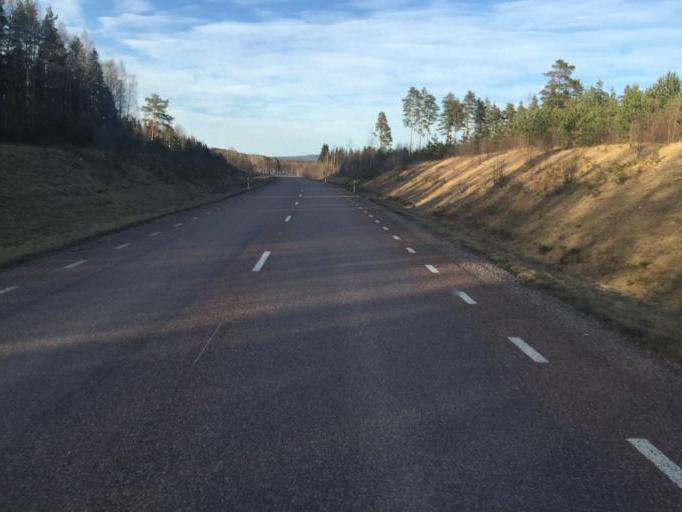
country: SE
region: Dalarna
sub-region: Gagnefs Kommun
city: Gagnef
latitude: 60.5400
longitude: 15.0557
